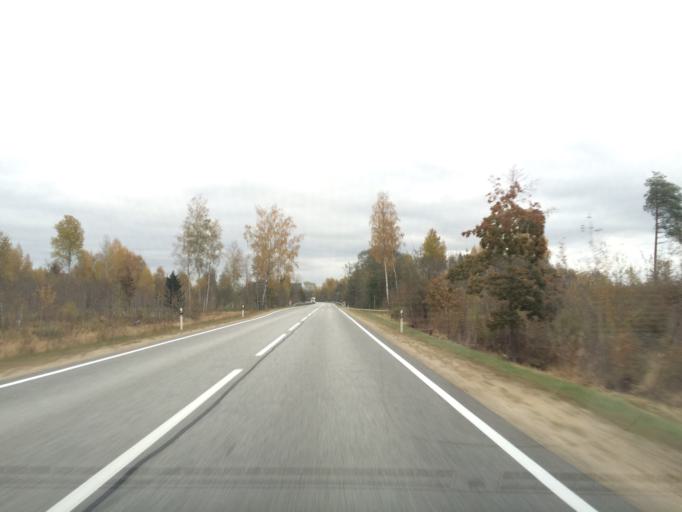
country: LV
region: Livani
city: Livani
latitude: 56.5298
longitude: 26.3630
